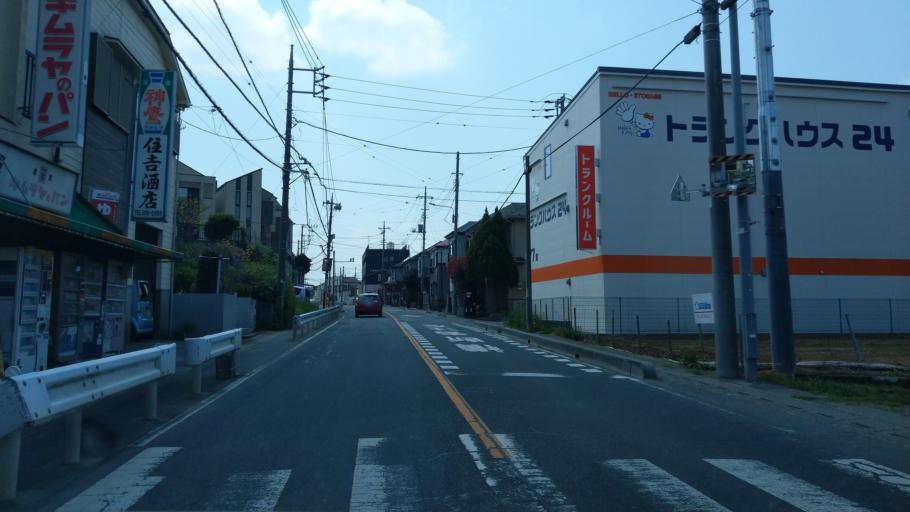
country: JP
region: Saitama
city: Saitama
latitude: 35.8893
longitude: 139.6633
